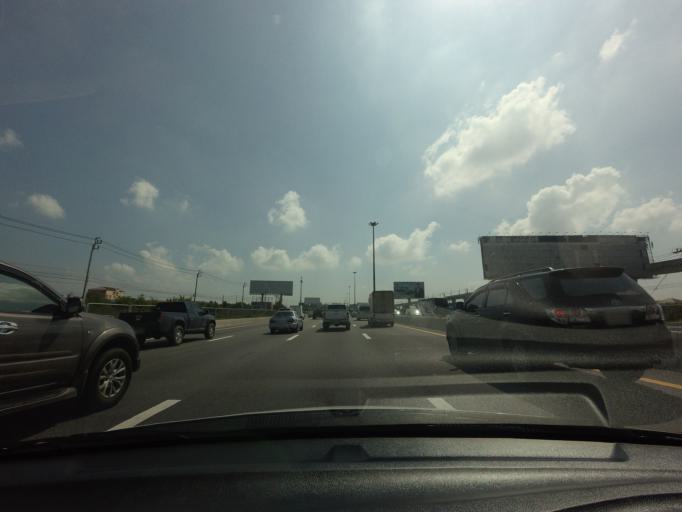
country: TH
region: Bangkok
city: Saphan Sung
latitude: 13.7314
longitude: 100.7147
